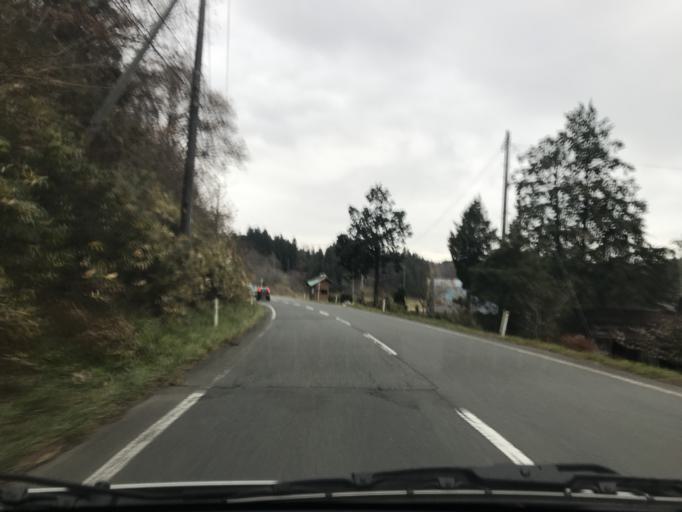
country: JP
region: Iwate
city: Mizusawa
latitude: 39.0348
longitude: 141.3394
